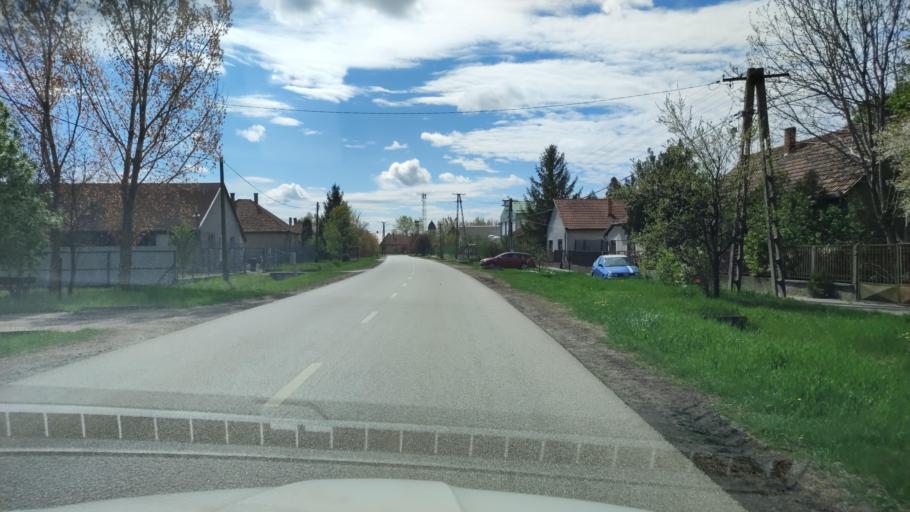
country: HU
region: Pest
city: Jaszkarajeno
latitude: 47.1011
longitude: 20.0210
